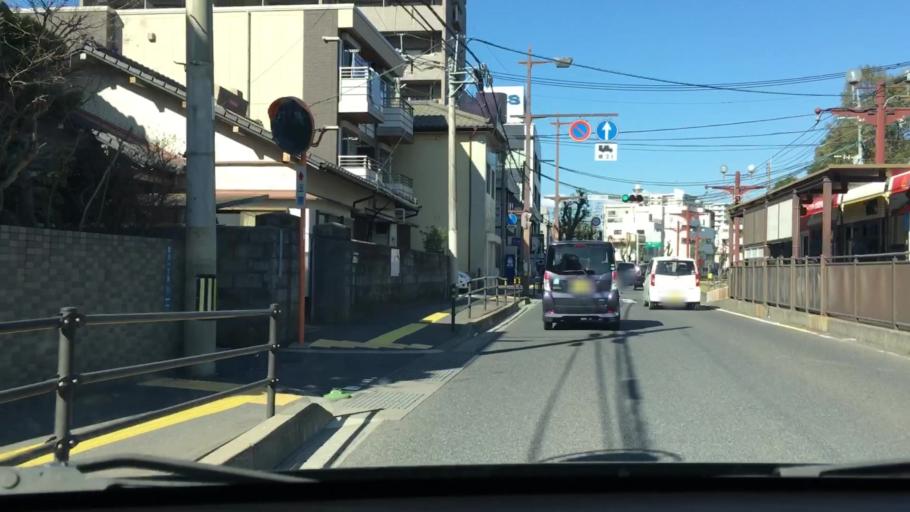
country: JP
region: Kagoshima
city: Kagoshima-shi
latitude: 31.5666
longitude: 130.5429
